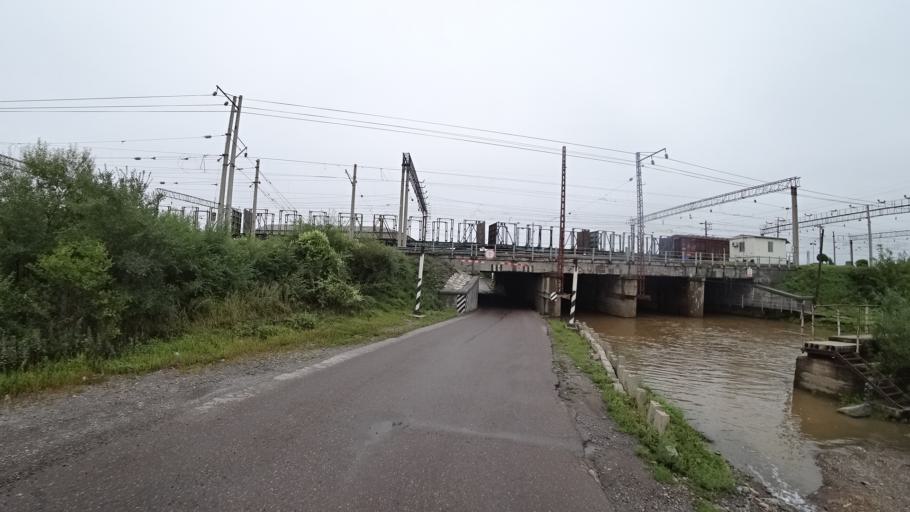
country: RU
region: Primorskiy
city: Monastyrishche
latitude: 44.2036
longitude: 132.4373
